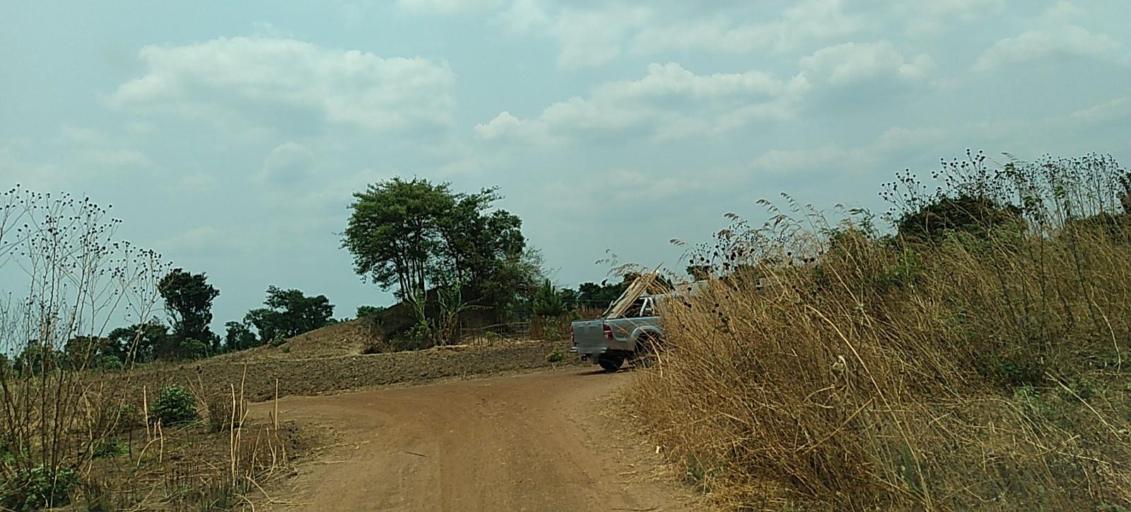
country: ZM
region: Copperbelt
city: Kalulushi
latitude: -12.7990
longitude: 28.0062
